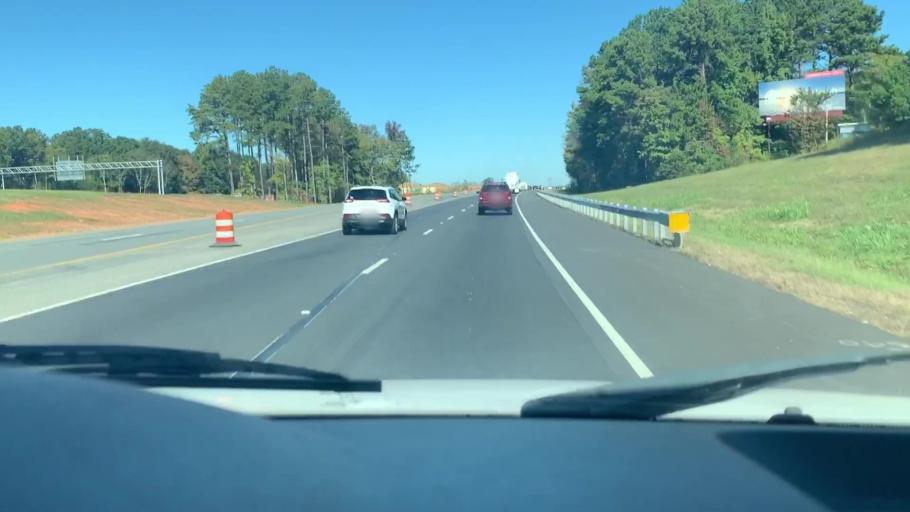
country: US
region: North Carolina
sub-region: Mecklenburg County
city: Huntersville
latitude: 35.4303
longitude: -80.8665
